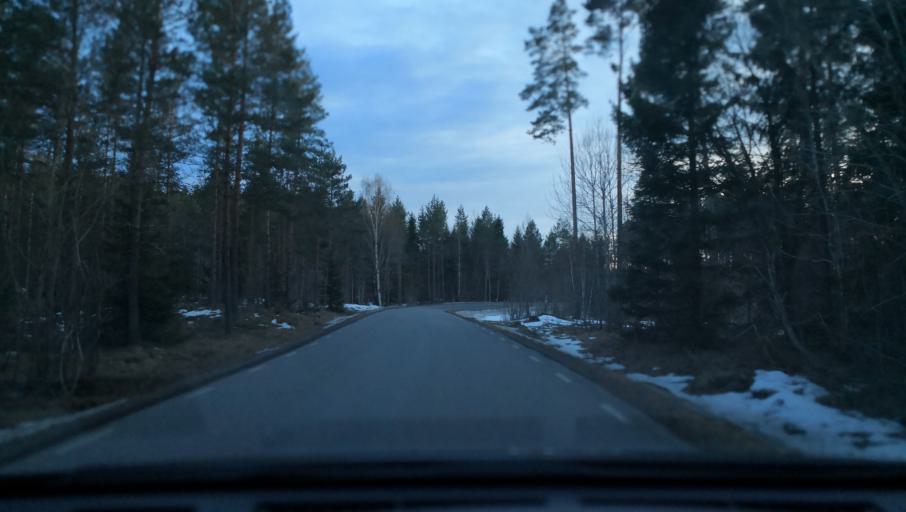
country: SE
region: Uppsala
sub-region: Osthammars Kommun
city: Osterbybruk
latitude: 60.2340
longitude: 17.9212
